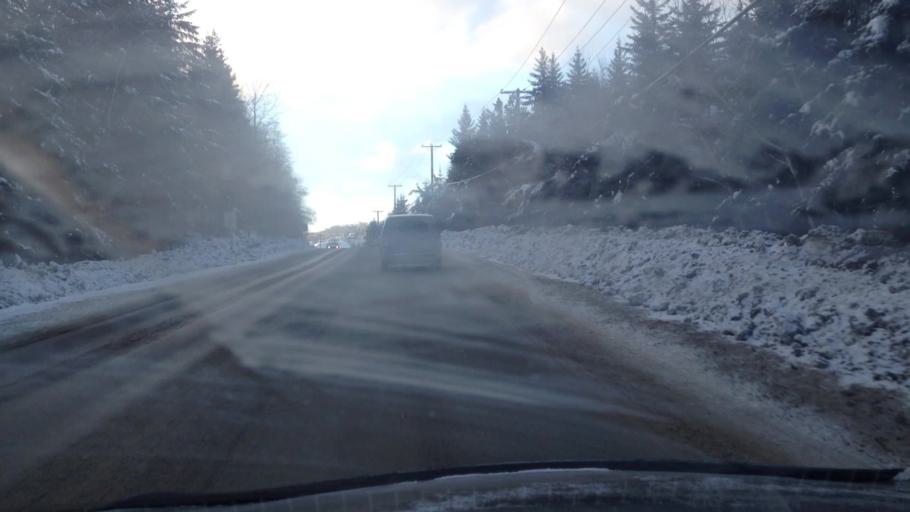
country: CA
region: Quebec
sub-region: Laurentides
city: Saint-Sauveur
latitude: 45.8883
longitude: -74.1395
